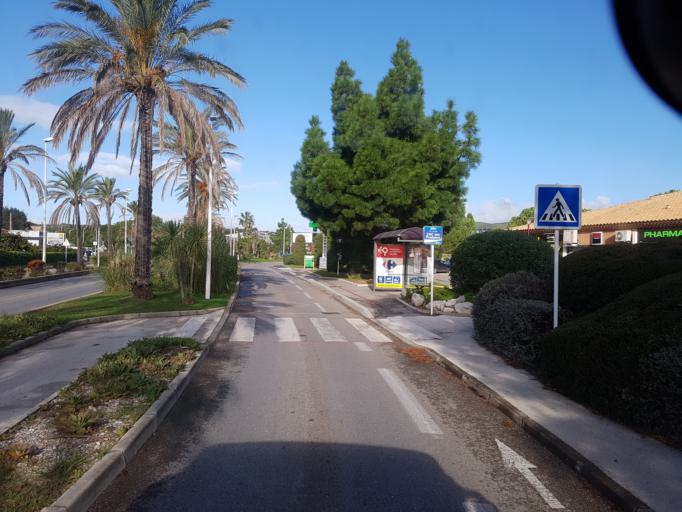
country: FR
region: Provence-Alpes-Cote d'Azur
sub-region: Departement du Var
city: Saint-Cyr-sur-Mer
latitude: 43.1821
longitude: 5.6956
